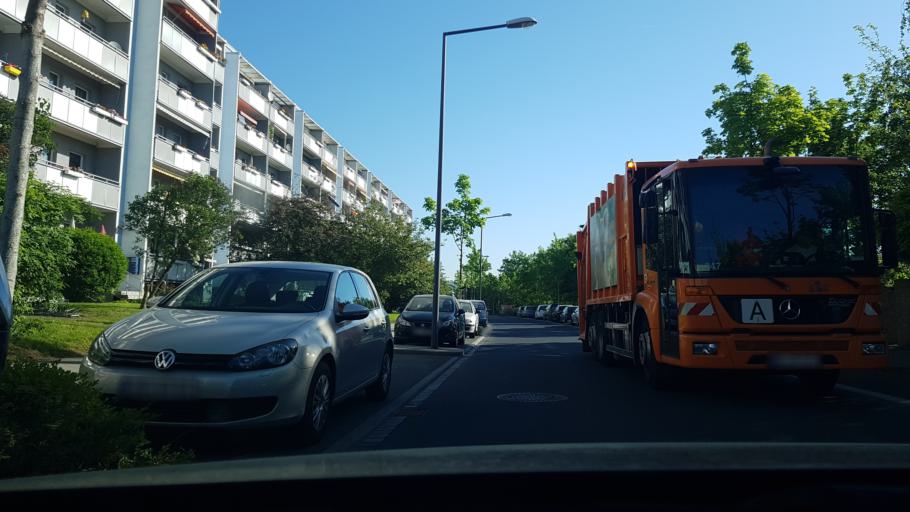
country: DE
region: Saxony
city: Heidenau
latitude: 51.0048
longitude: 13.8052
